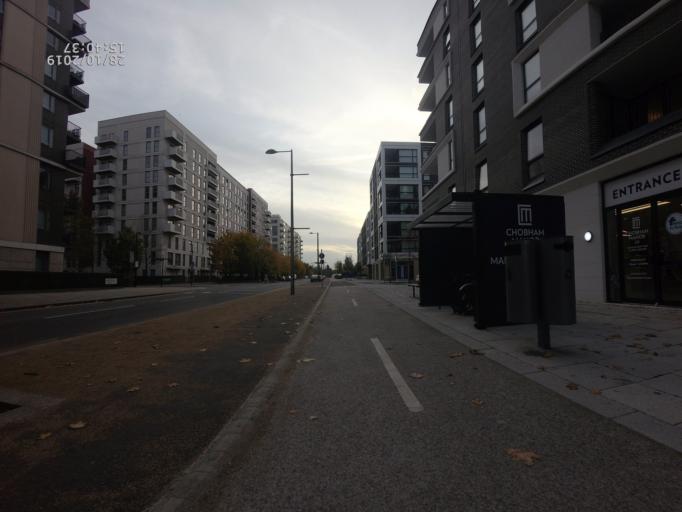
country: GB
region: England
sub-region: Greater London
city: Poplar
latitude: 51.5485
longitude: -0.0116
